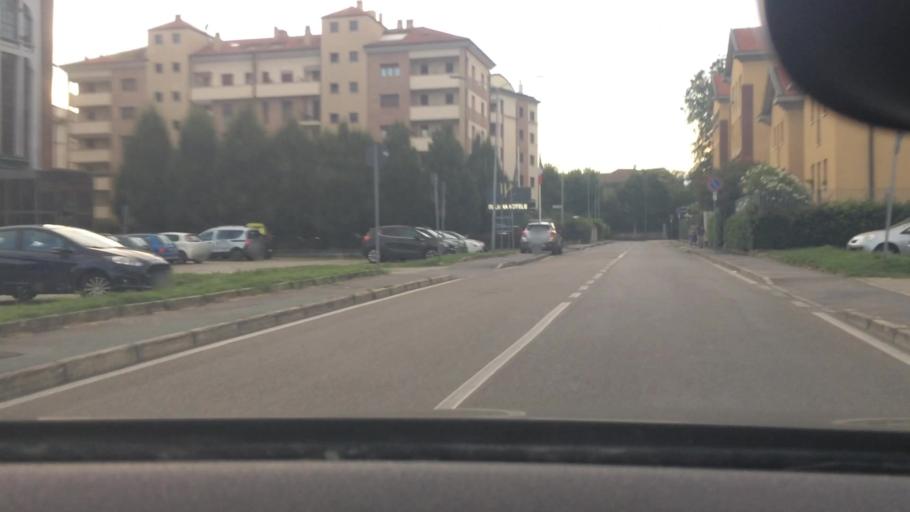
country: IT
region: Lombardy
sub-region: Citta metropolitana di Milano
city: Rho
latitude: 45.5237
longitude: 9.0384
